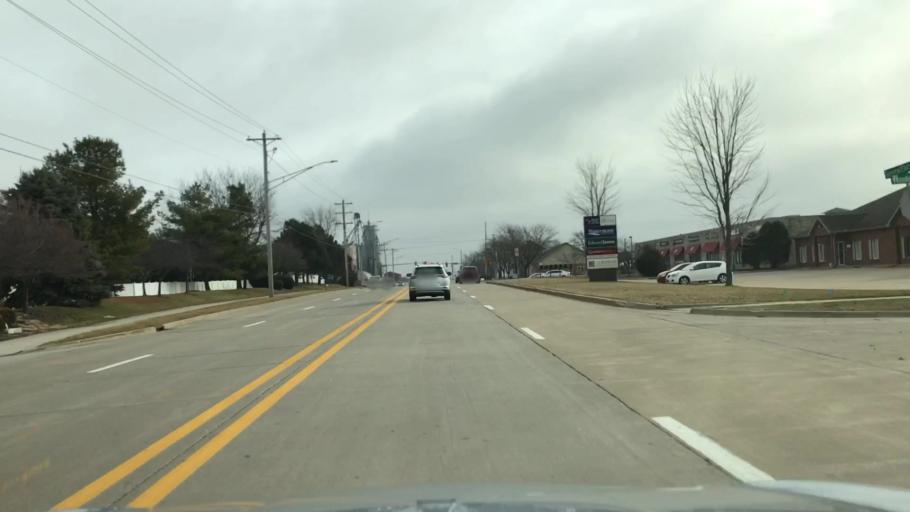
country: US
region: Illinois
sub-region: McLean County
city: Normal
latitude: 40.5027
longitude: -88.9067
